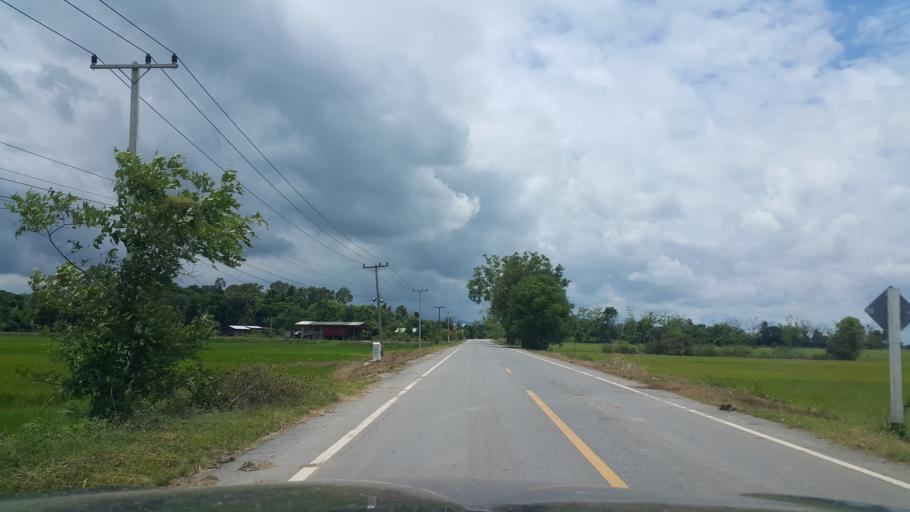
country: TH
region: Sukhothai
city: Kong Krailat
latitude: 16.9357
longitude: 99.9284
